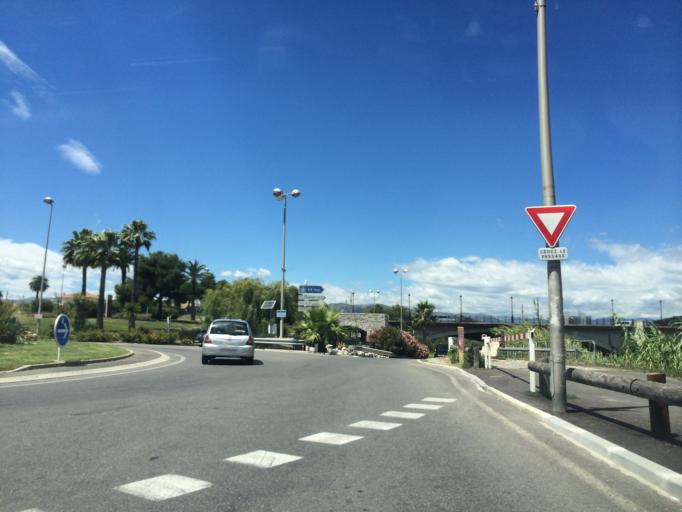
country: FR
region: Provence-Alpes-Cote d'Azur
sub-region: Departement des Alpes-Maritimes
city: Saint-Laurent-du-Var
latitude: 43.6622
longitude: 7.1981
